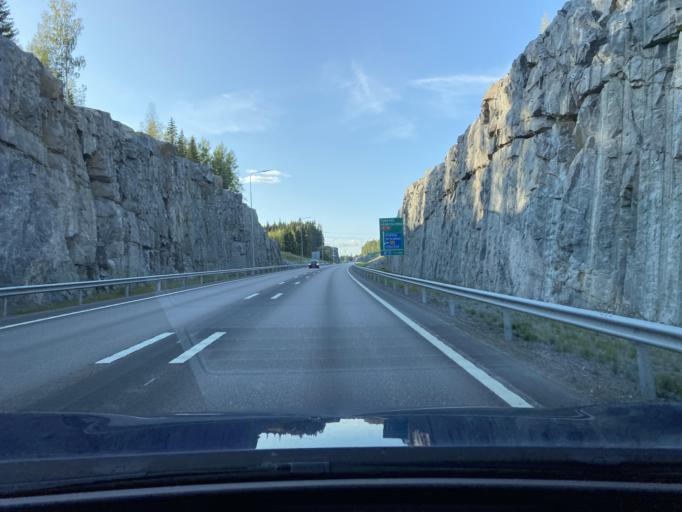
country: FI
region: Paijanne Tavastia
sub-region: Lahti
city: Hollola
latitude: 60.9673
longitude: 25.5158
